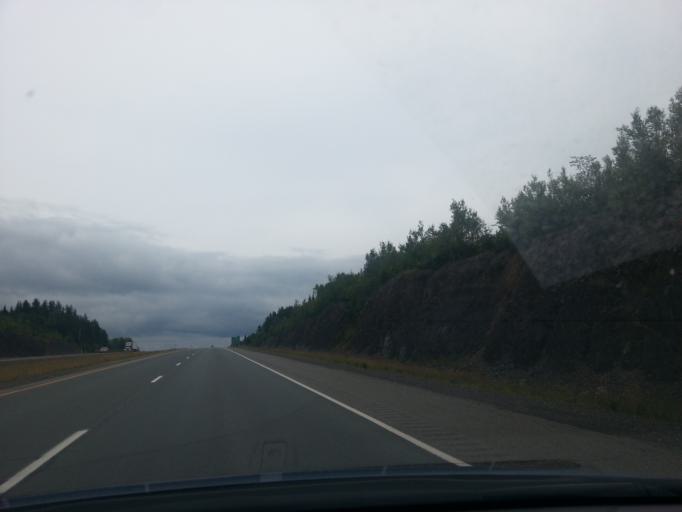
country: CA
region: New Brunswick
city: Harrison Brook
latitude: 47.2779
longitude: -68.0202
